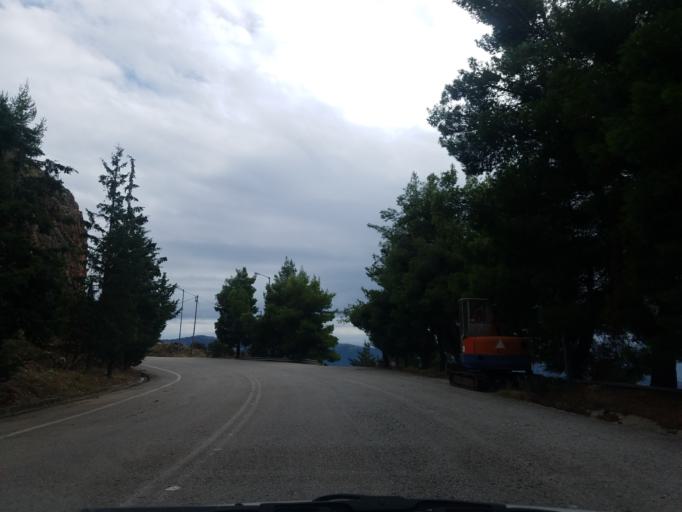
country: GR
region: Central Greece
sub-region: Nomos Voiotias
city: Arachova
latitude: 38.4816
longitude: 22.5767
